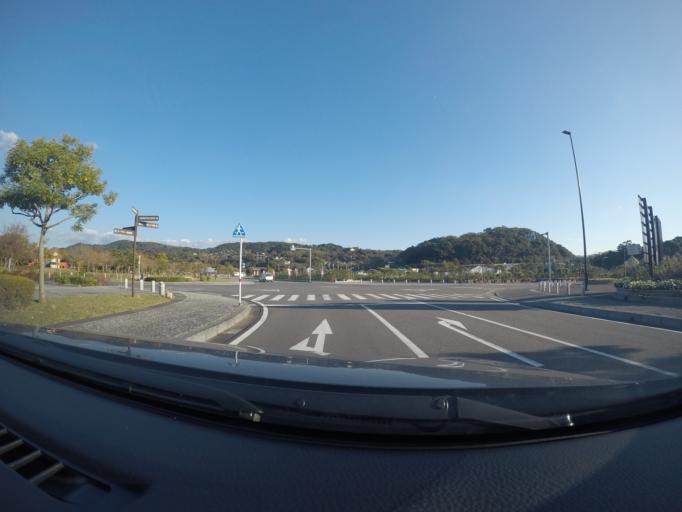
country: JP
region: Kumamoto
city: Minamata
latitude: 32.2004
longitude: 130.3822
